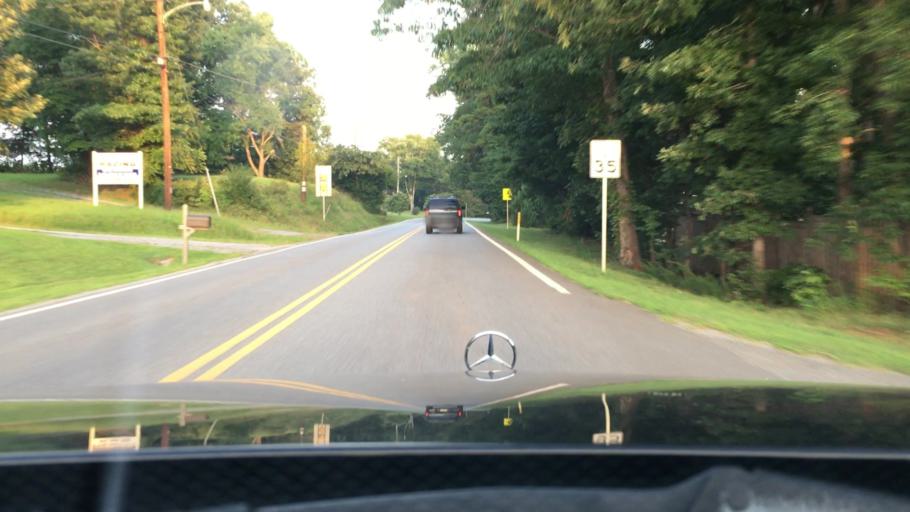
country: US
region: Virginia
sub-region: Campbell County
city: Altavista
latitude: 37.1310
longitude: -79.2817
